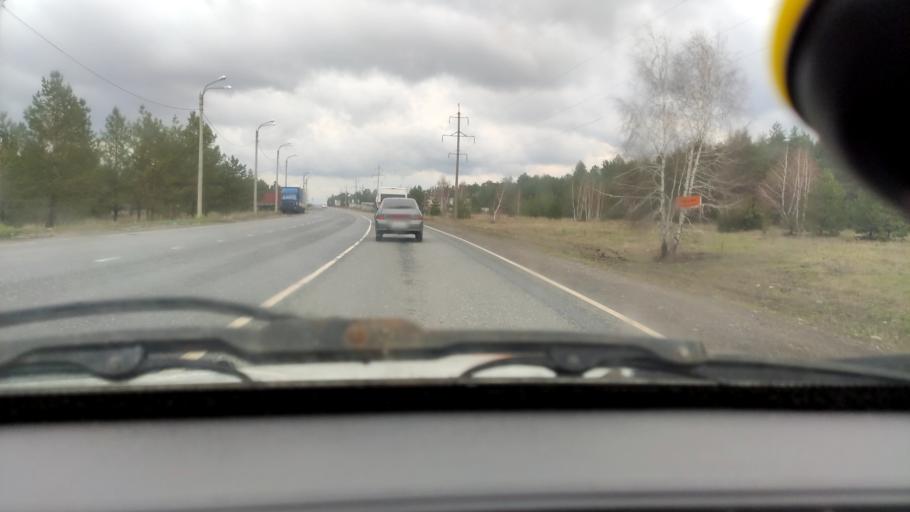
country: RU
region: Samara
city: Zhigulevsk
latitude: 53.5636
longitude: 49.5445
